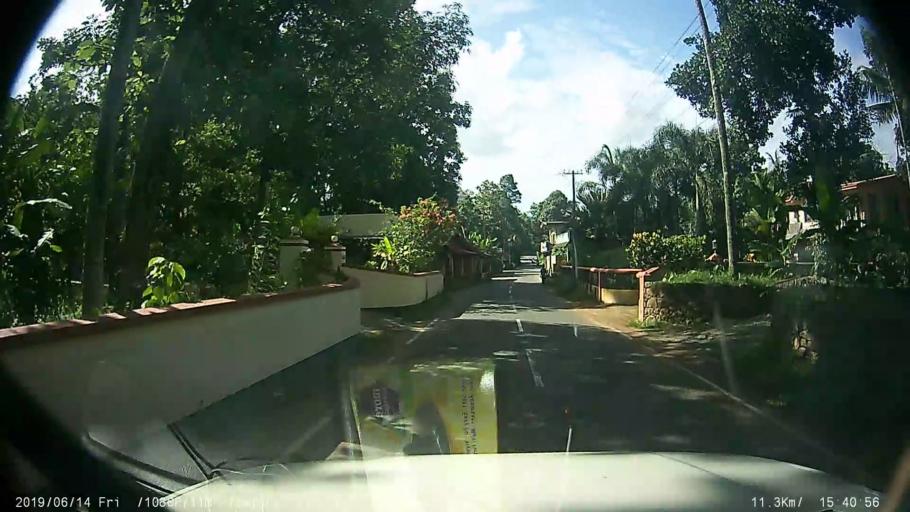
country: IN
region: Kerala
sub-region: Kottayam
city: Palackattumala
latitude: 9.7748
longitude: 76.6127
